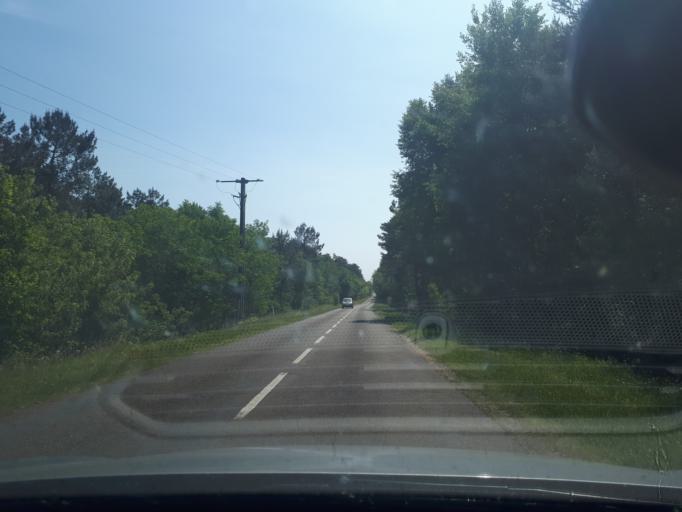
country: FR
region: Pays de la Loire
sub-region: Departement de la Sarthe
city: Saint-Mars-la-Briere
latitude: 48.0574
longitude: 0.3795
